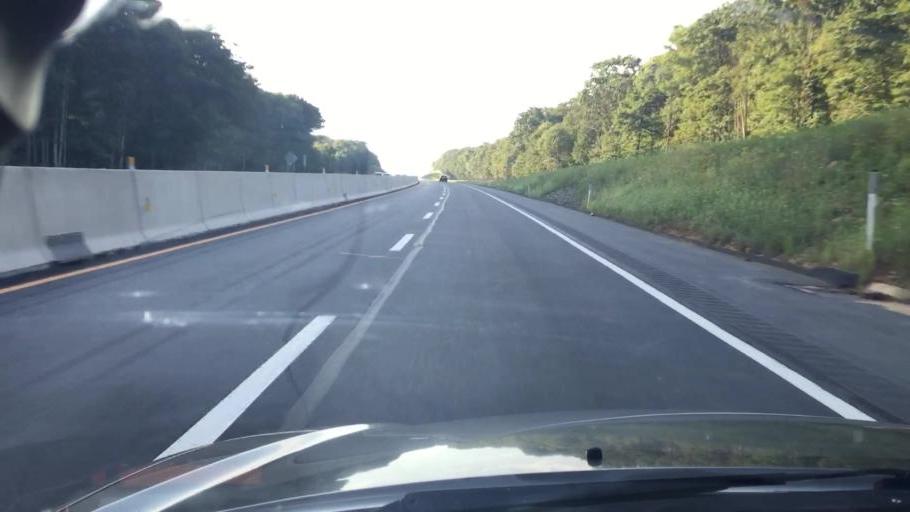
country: US
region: Pennsylvania
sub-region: Carbon County
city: Towamensing Trails
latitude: 41.0247
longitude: -75.6482
